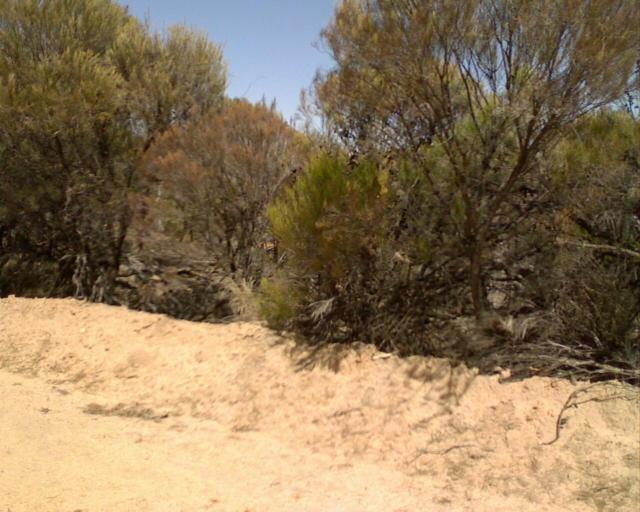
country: AU
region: Western Australia
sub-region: Wongan-Ballidu
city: Wongan Hills
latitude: -30.4275
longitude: 116.9669
